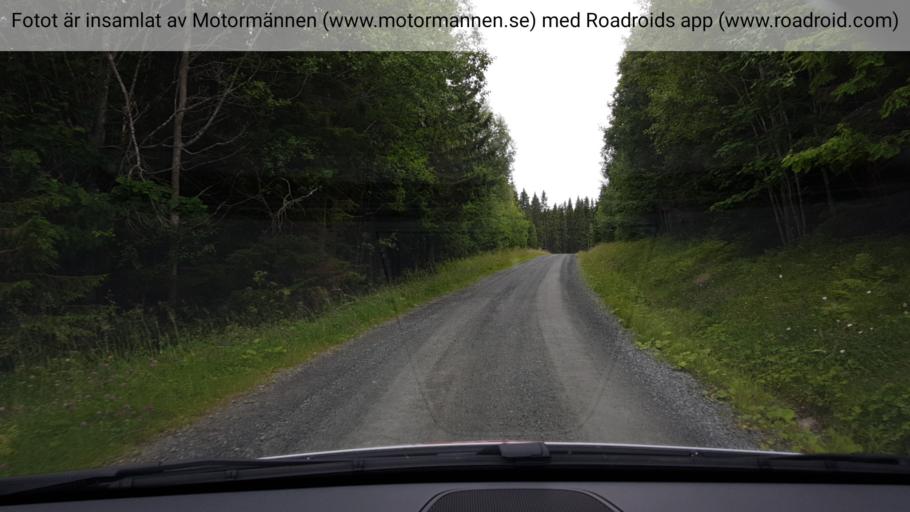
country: SE
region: Jaemtland
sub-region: Krokoms Kommun
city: Valla
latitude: 63.5909
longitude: 14.0014
